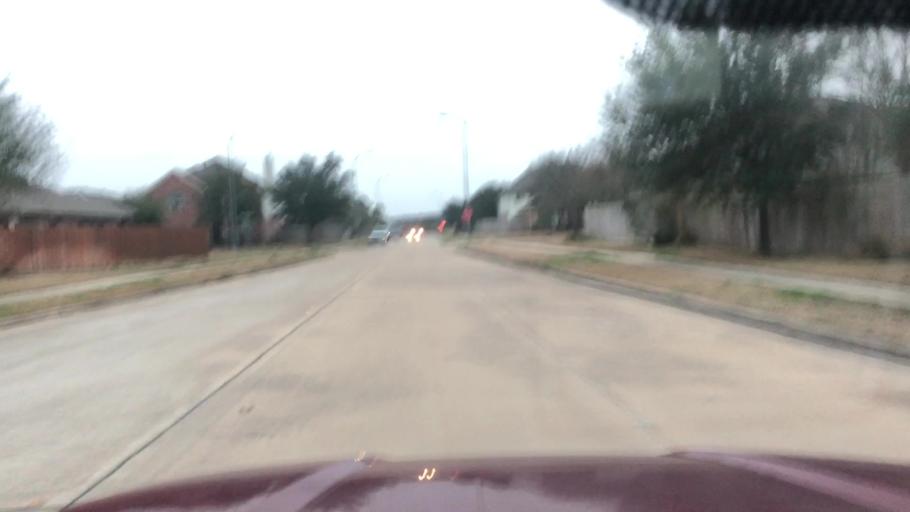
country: US
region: Texas
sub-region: Harris County
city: Tomball
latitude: 30.0857
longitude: -95.5554
